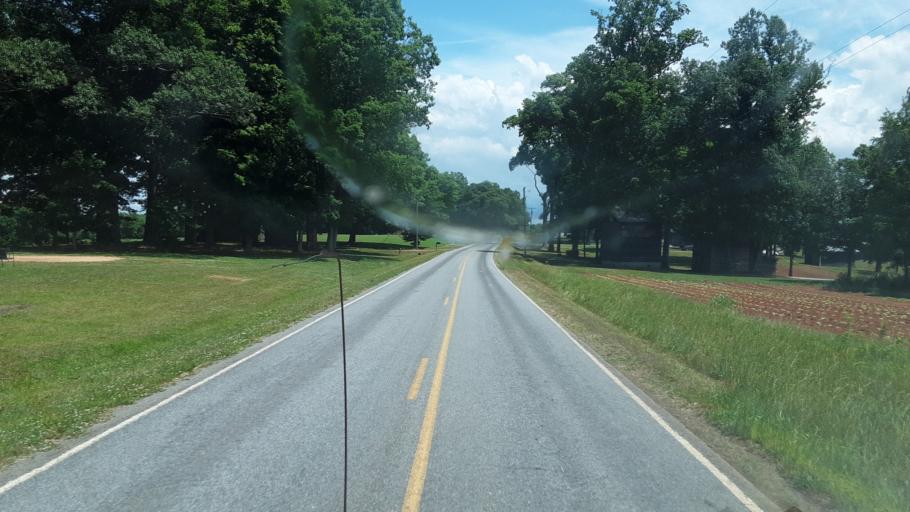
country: US
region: North Carolina
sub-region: Yadkin County
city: Jonesville
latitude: 36.0747
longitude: -80.8447
